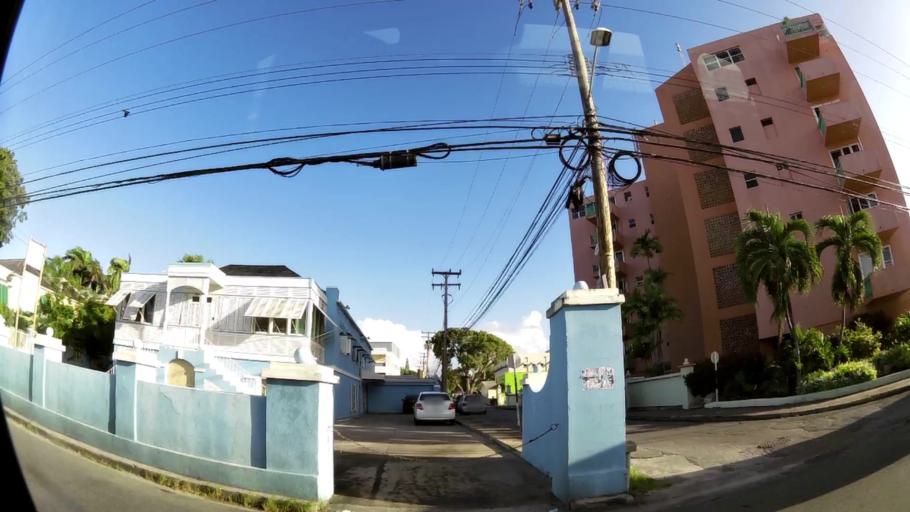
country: BB
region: Saint Michael
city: Bridgetown
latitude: 13.0743
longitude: -59.5981
